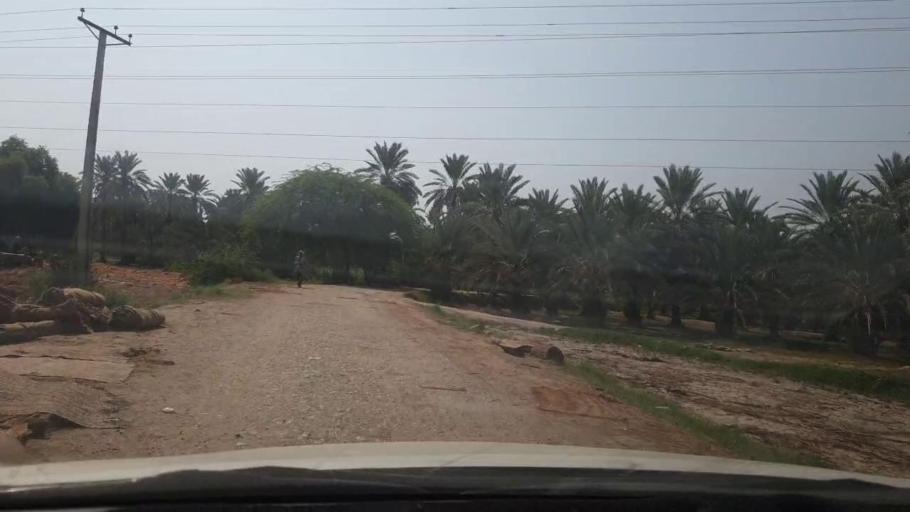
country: PK
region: Sindh
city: Rohri
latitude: 27.5922
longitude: 68.8521
